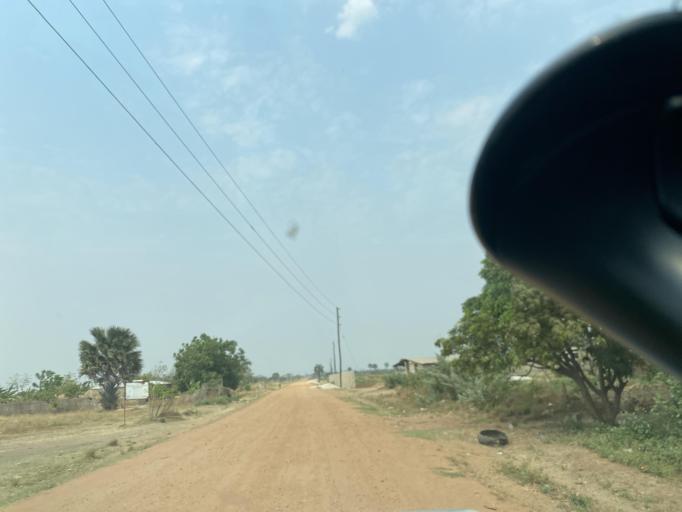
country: ZM
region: Lusaka
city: Kafue
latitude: -15.6724
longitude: 28.0178
